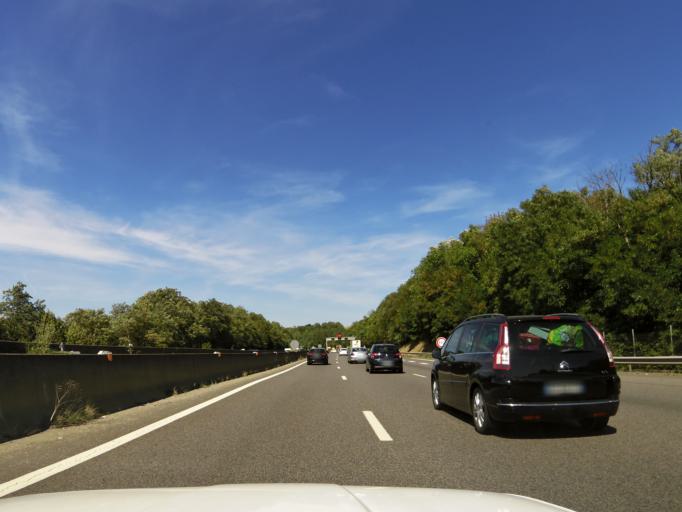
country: FR
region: Rhone-Alpes
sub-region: Departement de l'Isere
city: Reventin-Vaugris
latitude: 45.4809
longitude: 4.8336
